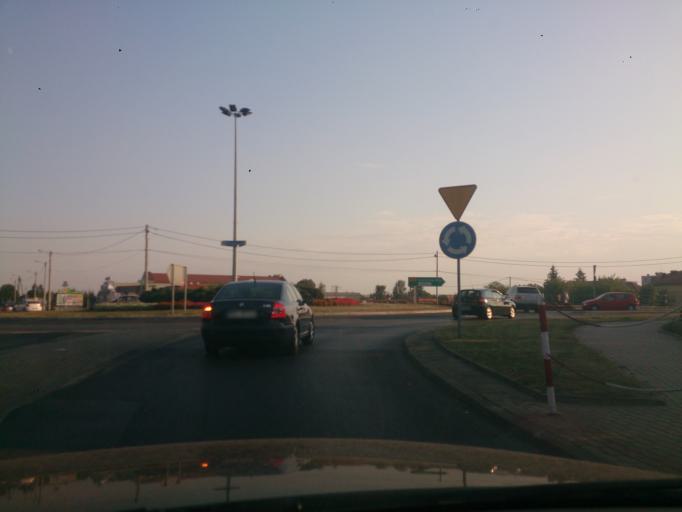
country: PL
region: Subcarpathian Voivodeship
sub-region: Powiat kolbuszowski
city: Kolbuszowa
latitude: 50.2445
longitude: 21.7785
